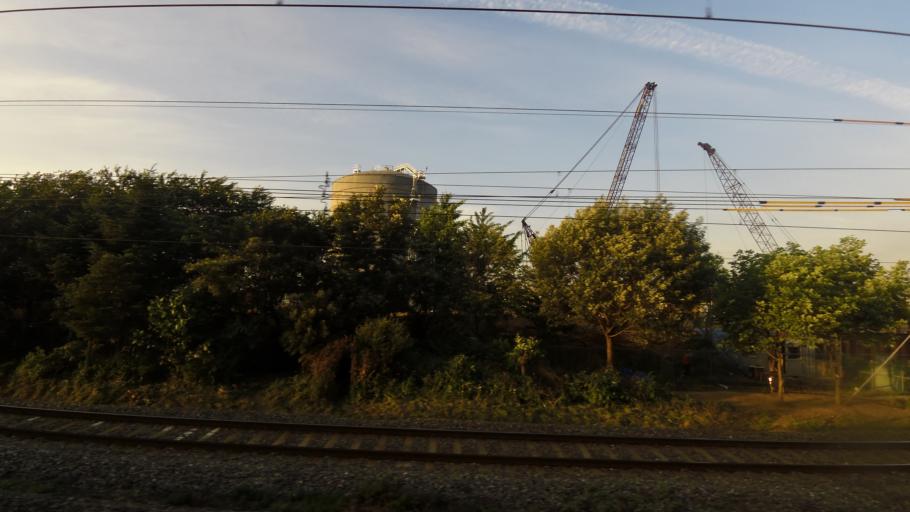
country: KR
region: Gyeonggi-do
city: Osan
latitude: 37.0389
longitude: 127.0661
